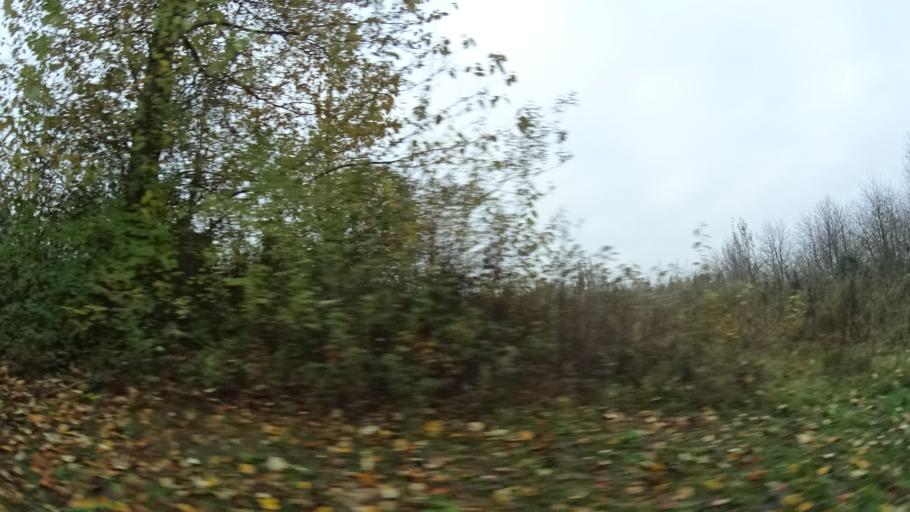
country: DE
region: Baden-Wuerttemberg
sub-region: Karlsruhe Region
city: Sinzheim
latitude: 48.7539
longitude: 8.1764
